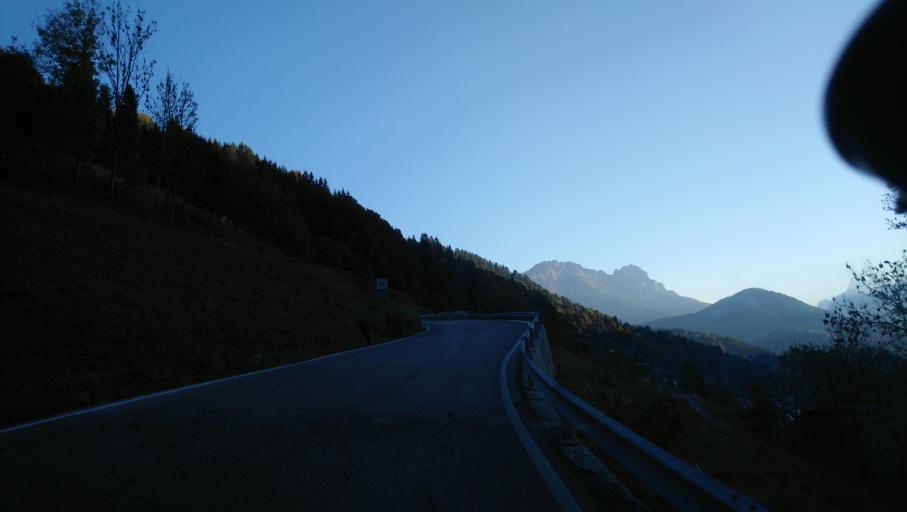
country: IT
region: Veneto
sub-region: Provincia di Belluno
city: Falcade Alto
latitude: 46.3543
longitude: 11.8599
